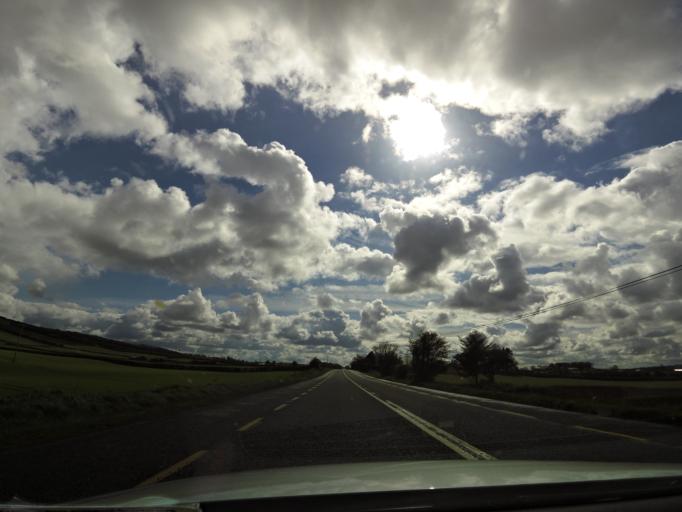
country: IE
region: Leinster
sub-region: Laois
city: Rathdowney
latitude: 52.8127
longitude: -7.4846
